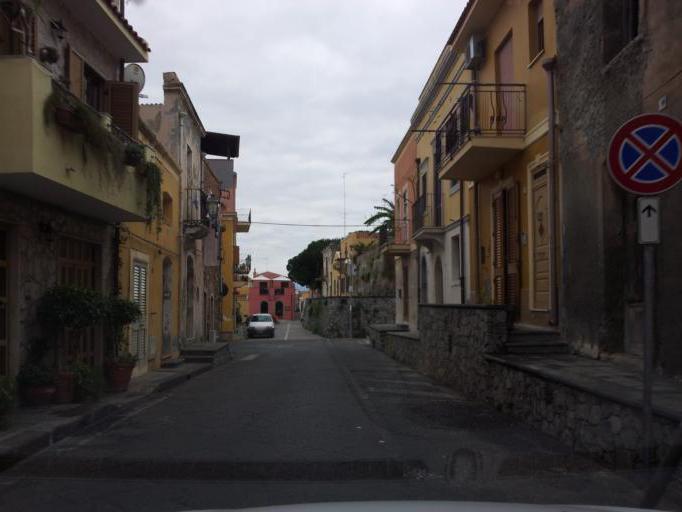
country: IT
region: Sicily
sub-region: Messina
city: Milazzo
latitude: 38.2306
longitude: 15.2435
